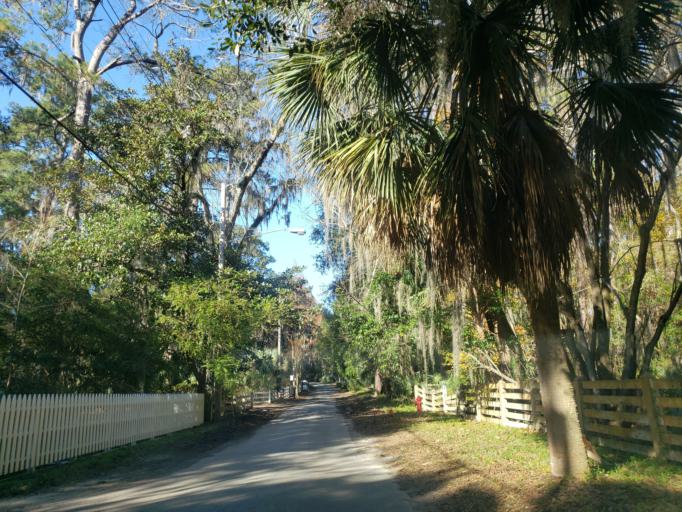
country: US
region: Georgia
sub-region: Chatham County
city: Montgomery
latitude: 31.9661
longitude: -81.1210
